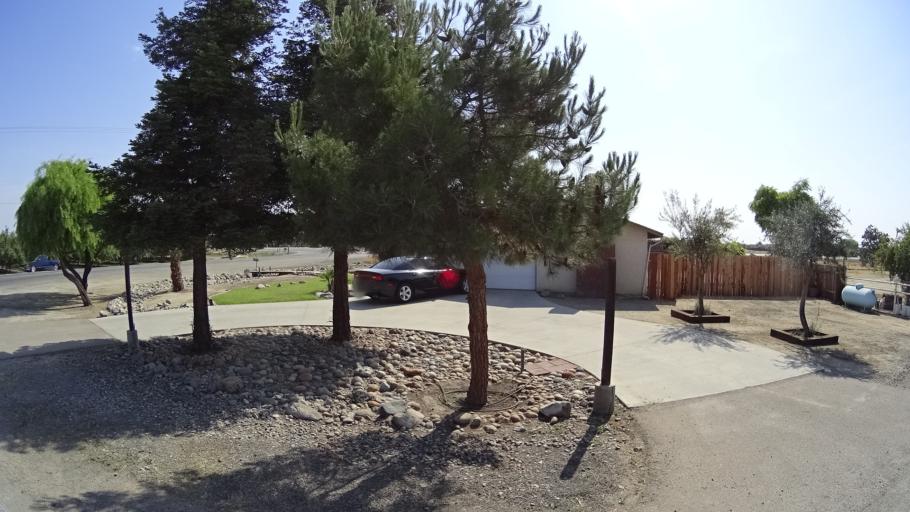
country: US
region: California
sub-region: Kings County
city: Lemoore
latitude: 36.3130
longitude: -119.8090
